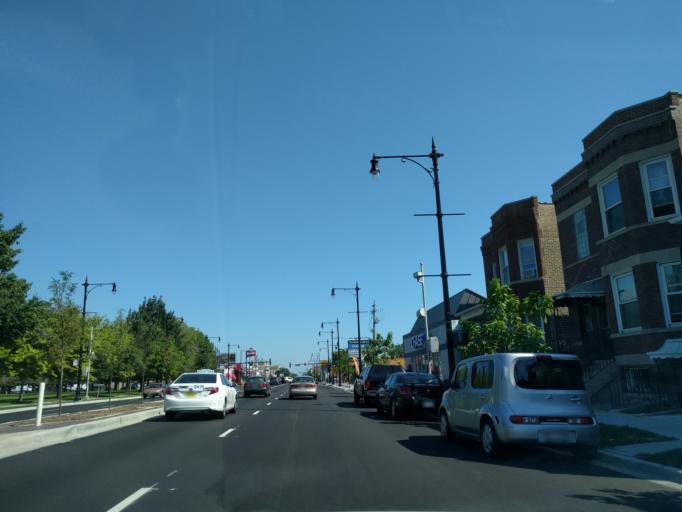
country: US
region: Illinois
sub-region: Cook County
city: Lincolnwood
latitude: 41.9454
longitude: -87.6881
